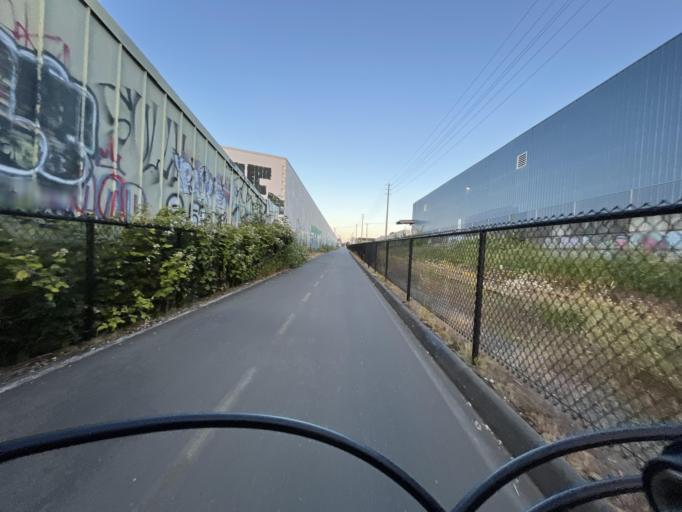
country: CA
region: British Columbia
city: Victoria
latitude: 48.4366
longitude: -123.4013
